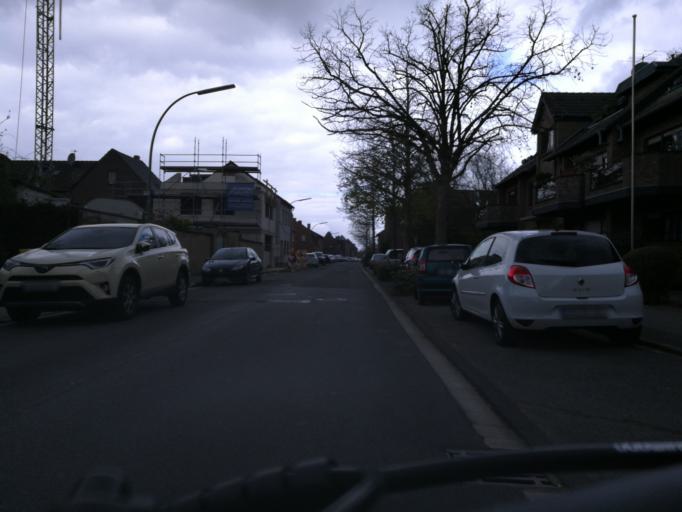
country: DE
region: North Rhine-Westphalia
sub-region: Regierungsbezirk Dusseldorf
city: Dusseldorf
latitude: 51.1642
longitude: 6.7873
